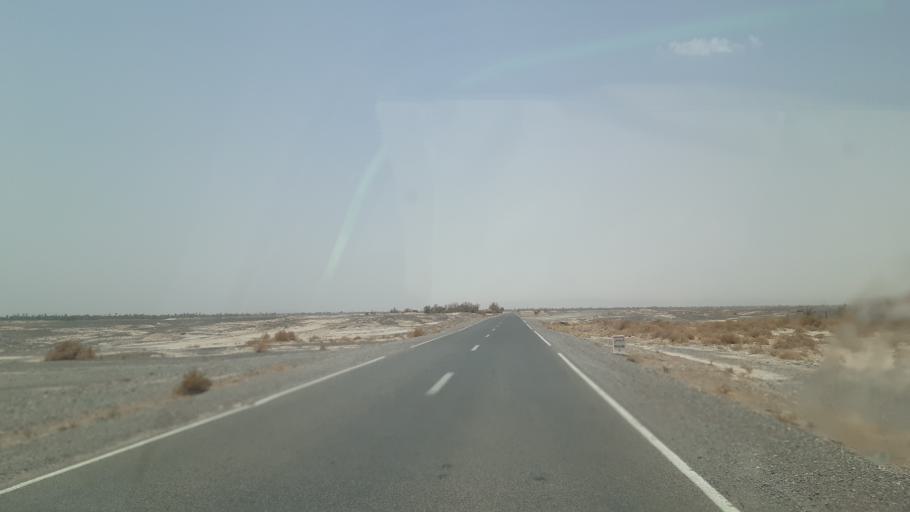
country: MA
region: Meknes-Tafilalet
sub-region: Errachidia
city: Jorf
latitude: 31.2707
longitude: -4.1655
